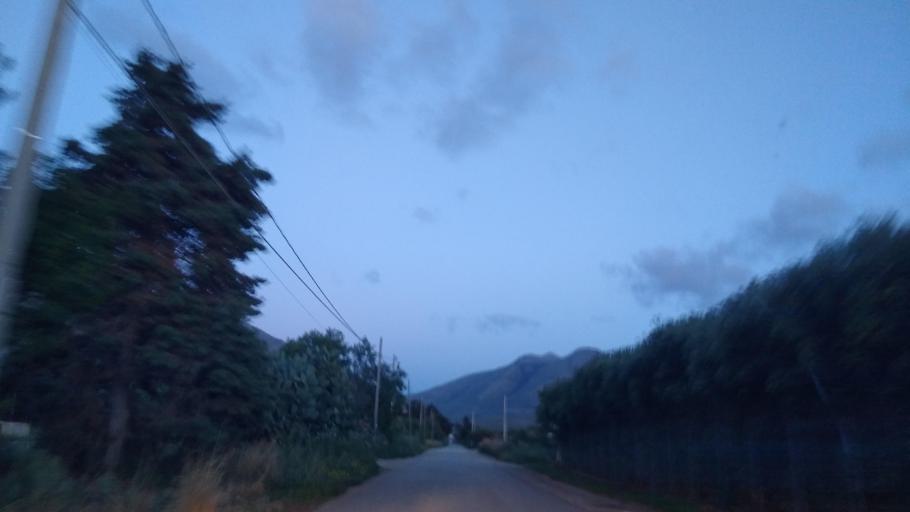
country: IT
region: Sicily
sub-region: Trapani
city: Castelluzzo
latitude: 38.1079
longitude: 12.7278
